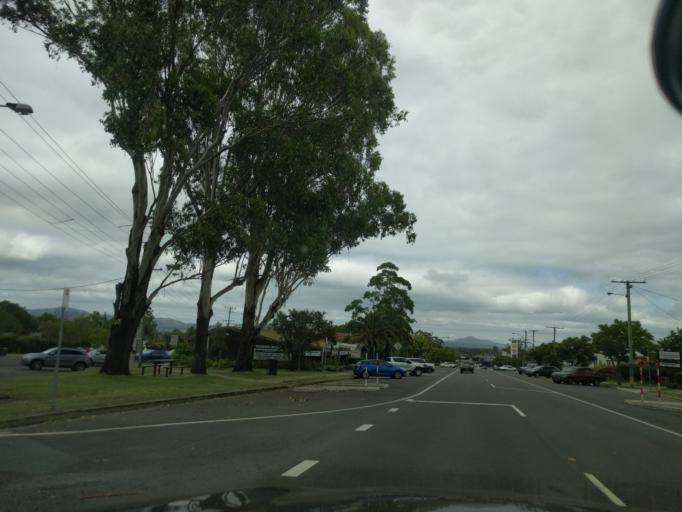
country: AU
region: Queensland
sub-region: Logan
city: Cedar Vale
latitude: -27.9911
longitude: 153.0010
